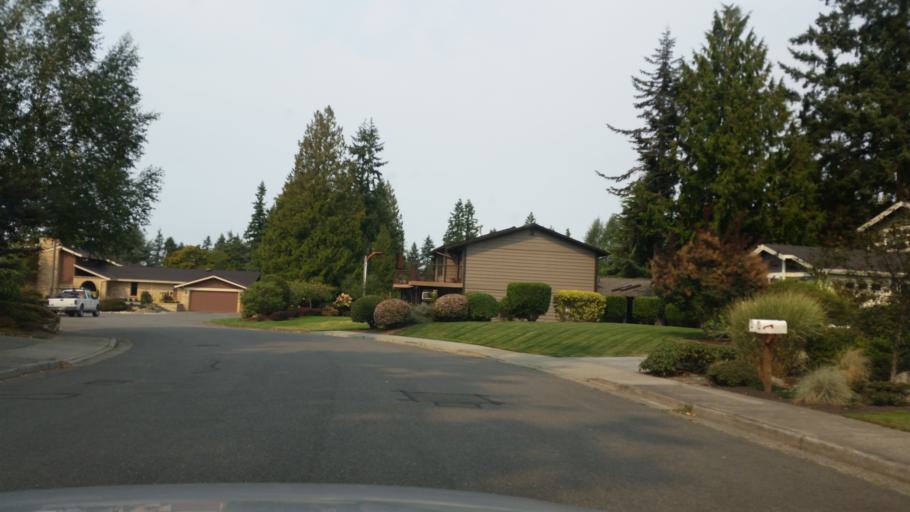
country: US
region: Washington
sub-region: Snohomish County
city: Edmonds
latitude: 47.8156
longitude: -122.3563
